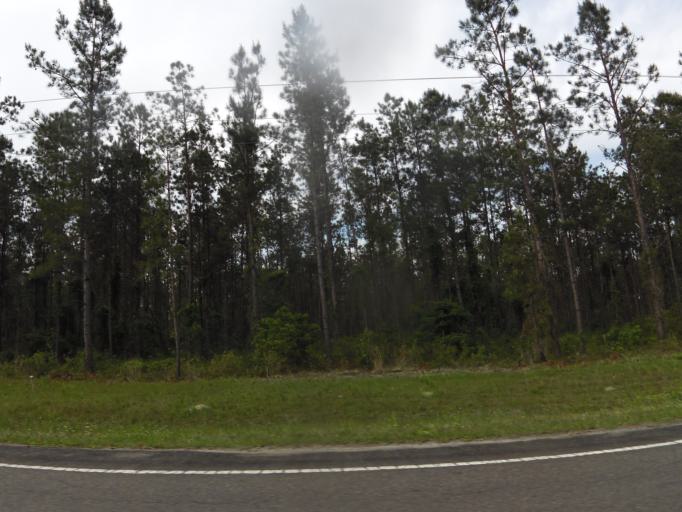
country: US
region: Florida
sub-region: Nassau County
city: Hilliard
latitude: 30.6944
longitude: -81.8341
